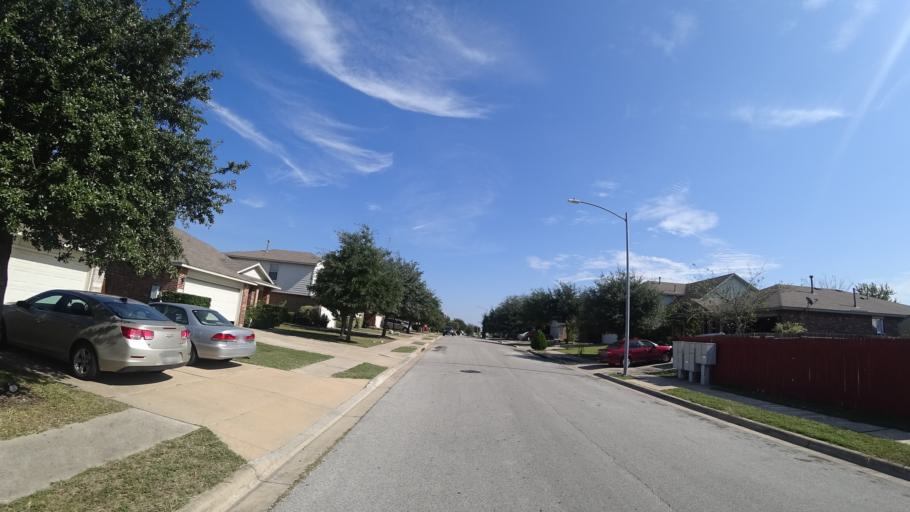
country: US
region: Texas
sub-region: Travis County
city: Pflugerville
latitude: 30.4286
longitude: -97.6401
